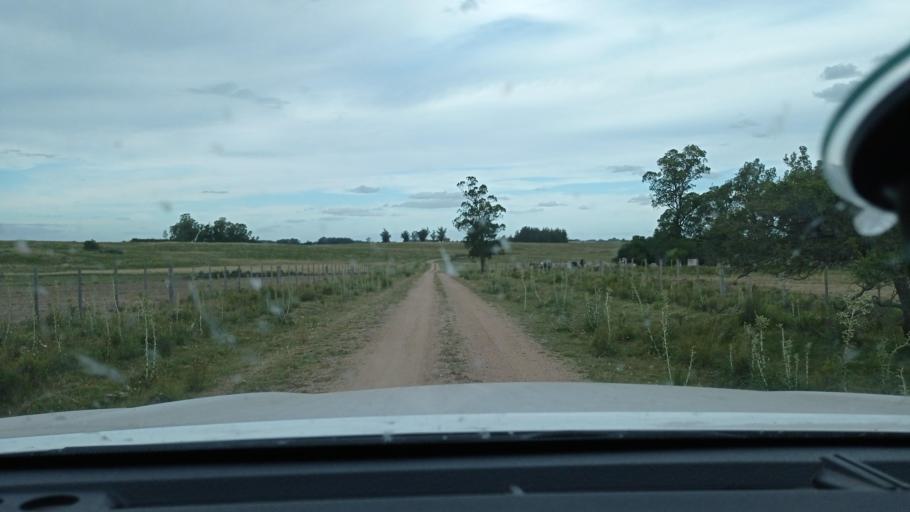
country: UY
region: Florida
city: Casupa
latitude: -34.1244
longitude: -55.8079
